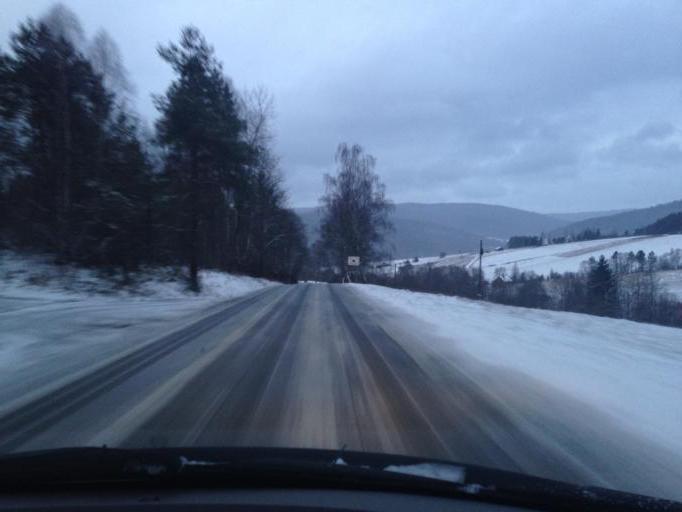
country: PL
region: Subcarpathian Voivodeship
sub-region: Powiat jasielski
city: Krempna
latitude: 49.5243
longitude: 21.5020
